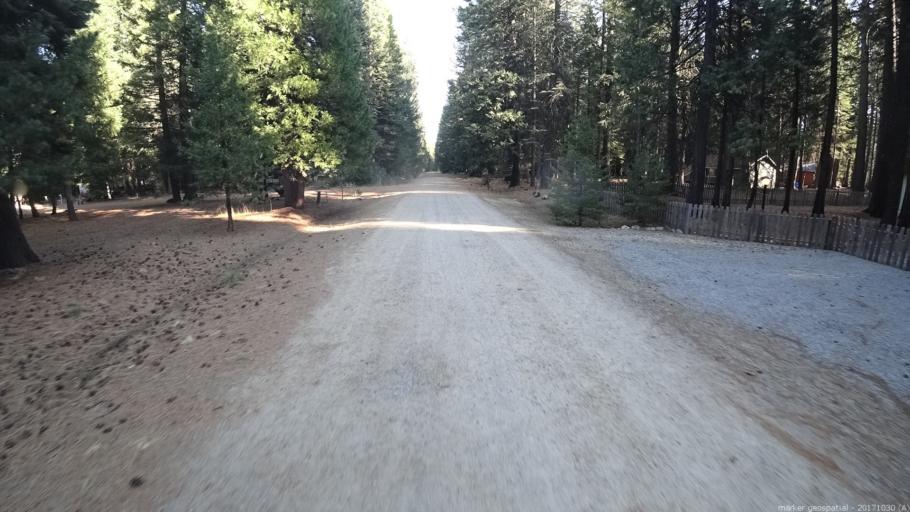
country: US
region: California
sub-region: Shasta County
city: Shingletown
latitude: 40.5582
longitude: -121.7314
